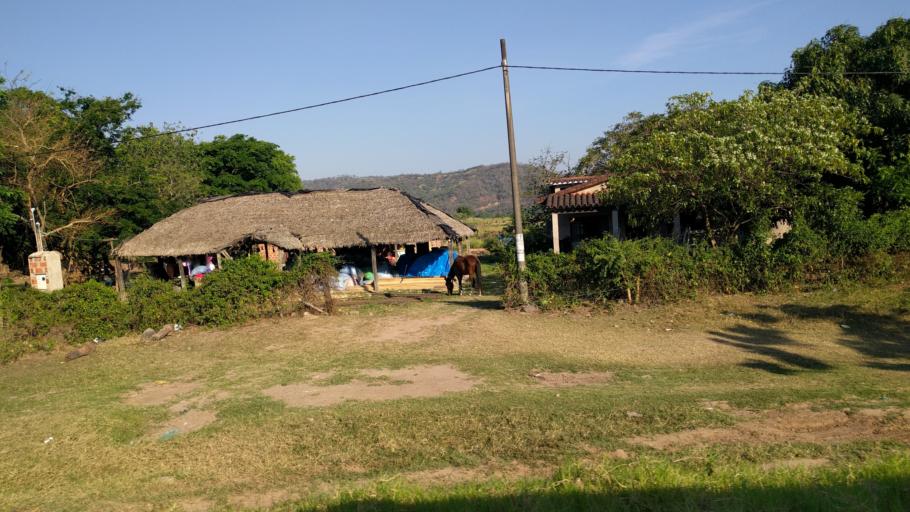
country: BO
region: Santa Cruz
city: Jorochito
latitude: -18.1386
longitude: -63.4770
